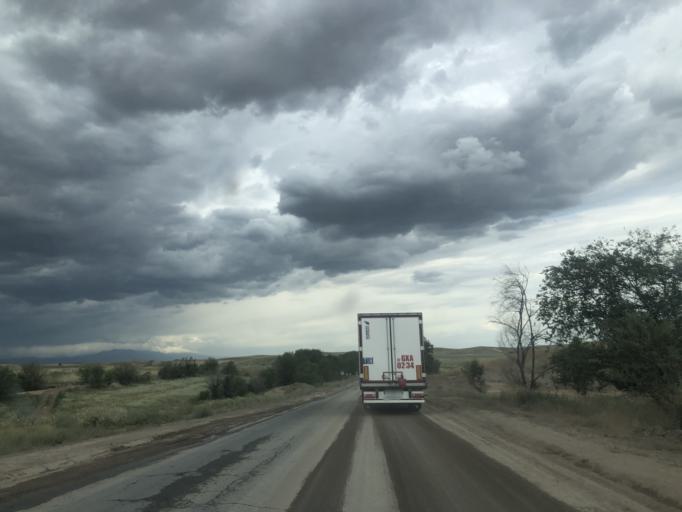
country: KG
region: Chuy
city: Bystrovka
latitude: 43.3225
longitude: 75.9254
